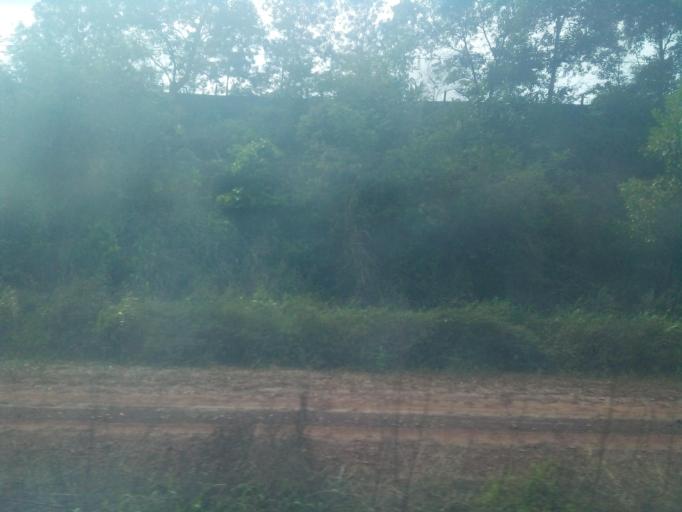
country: BR
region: Maranhao
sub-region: Sao Luis
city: Sao Luis
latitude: -2.7033
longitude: -44.3126
